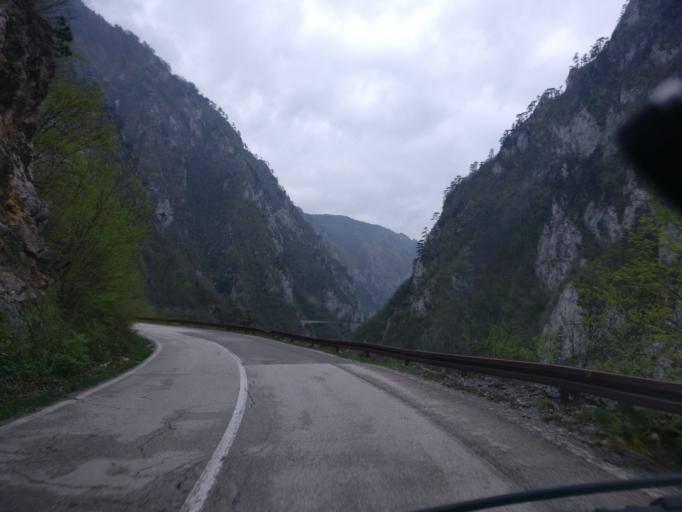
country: ME
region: Opstina Pluzine
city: Pluzine
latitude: 43.3018
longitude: 18.8514
